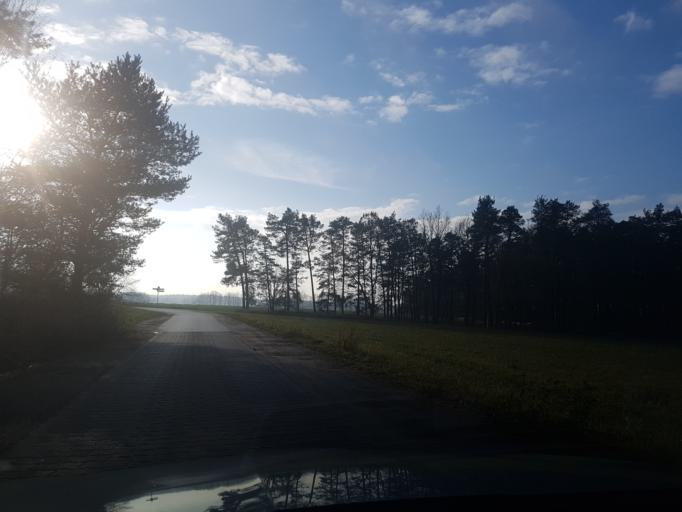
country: DE
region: Brandenburg
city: Ruckersdorf
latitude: 51.5391
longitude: 13.6058
